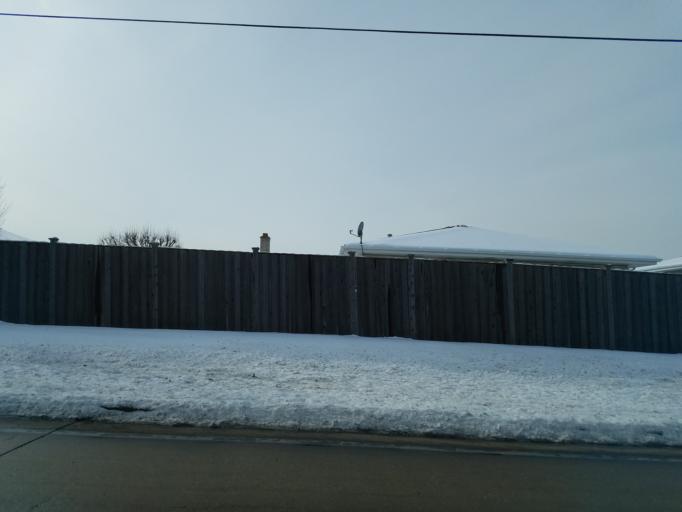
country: US
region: Illinois
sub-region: Cook County
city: Orland Hills
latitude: 41.5956
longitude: -87.8135
